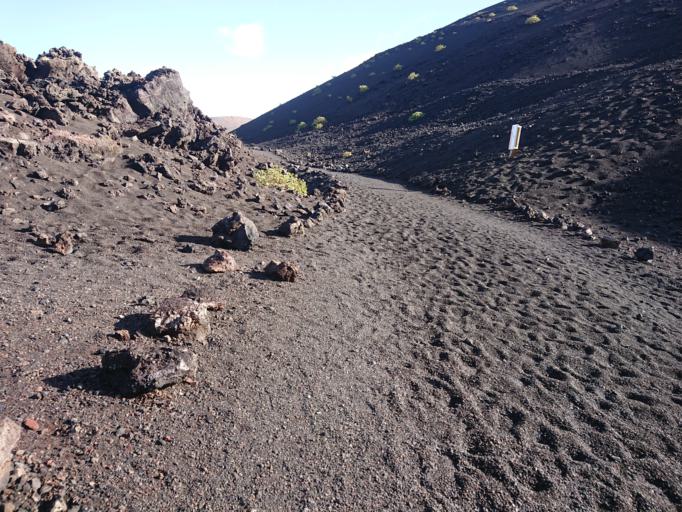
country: ES
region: Canary Islands
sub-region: Provincia de Las Palmas
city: Tias
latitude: 28.9916
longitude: -13.6958
